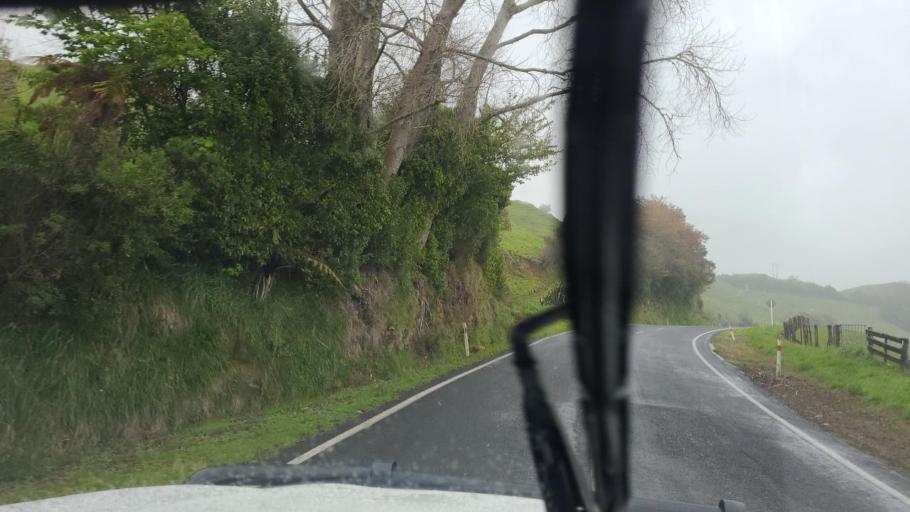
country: NZ
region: Taranaki
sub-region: South Taranaki District
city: Eltham
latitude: -39.2961
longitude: 174.4879
